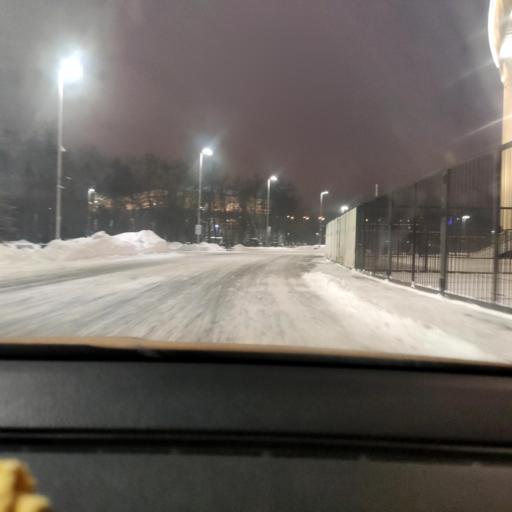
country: RU
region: Moscow
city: Luzhniki
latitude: 55.7160
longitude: 37.5563
